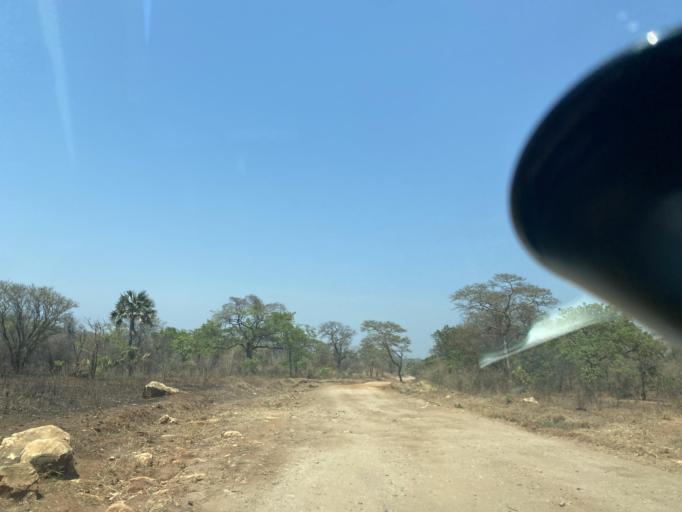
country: ZM
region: Lusaka
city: Lusaka
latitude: -15.5296
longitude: 28.0982
